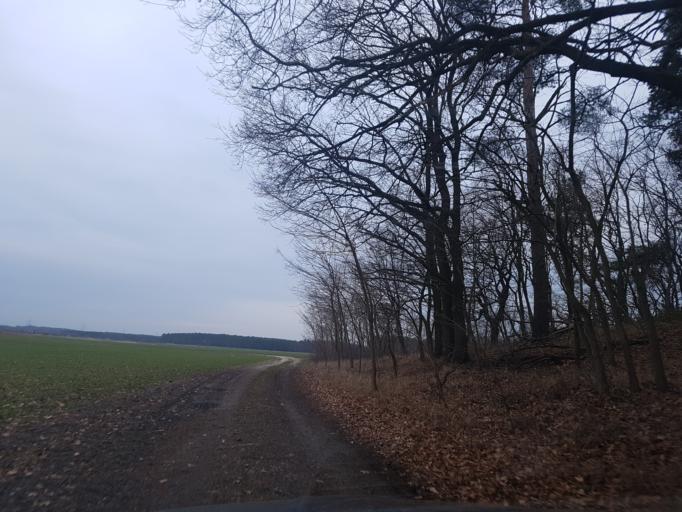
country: DE
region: Brandenburg
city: Bad Liebenwerda
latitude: 51.5514
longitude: 13.3841
